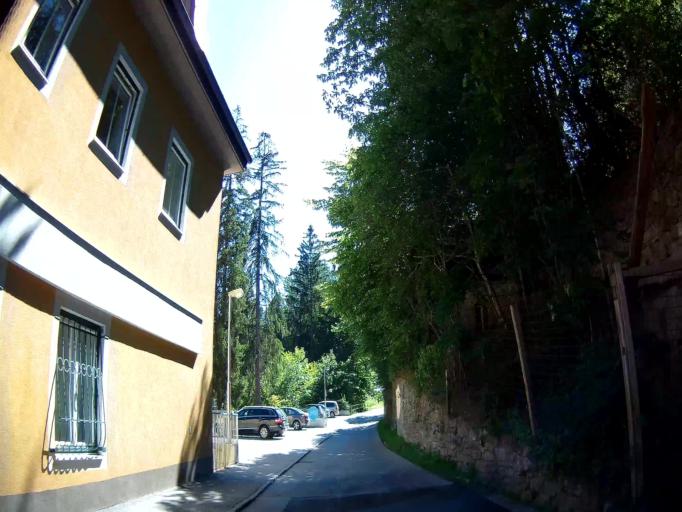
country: AT
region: Salzburg
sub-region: Politischer Bezirk Sankt Johann im Pongau
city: Bad Gastein
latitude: 47.1161
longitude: 13.1340
